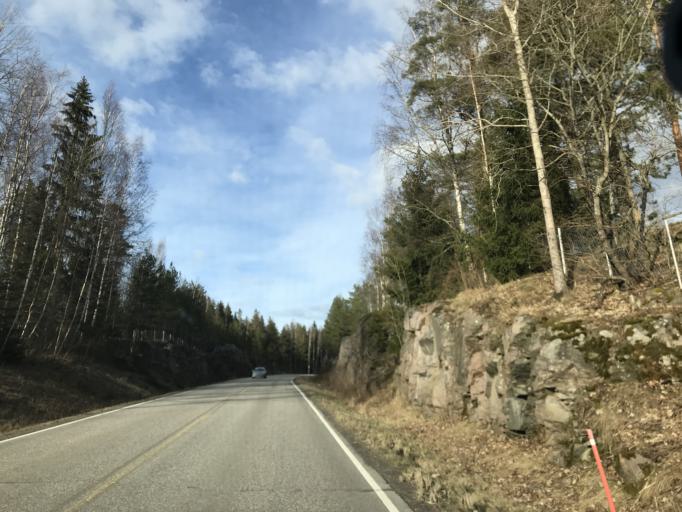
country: FI
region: Uusimaa
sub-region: Raaseporin
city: Ekenaes
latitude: 60.0779
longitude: 23.3518
